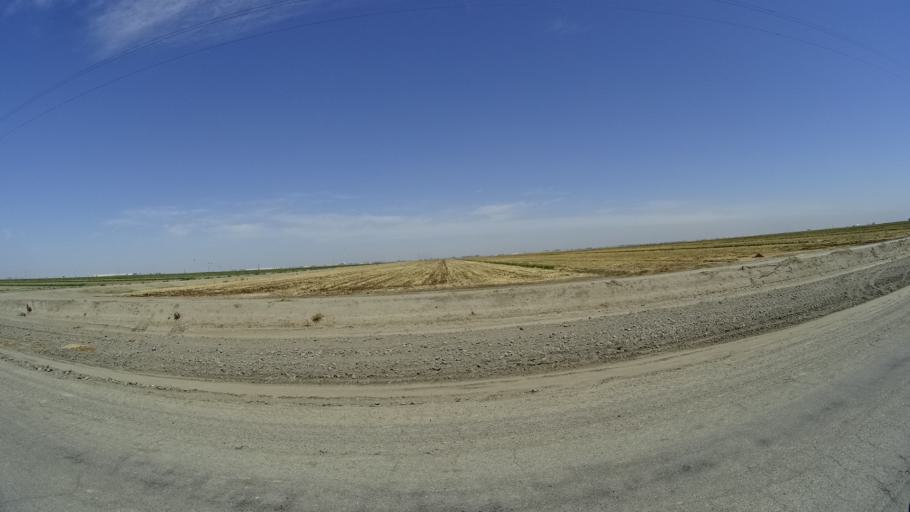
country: US
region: California
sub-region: Kings County
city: Corcoran
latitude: 36.1379
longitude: -119.6631
